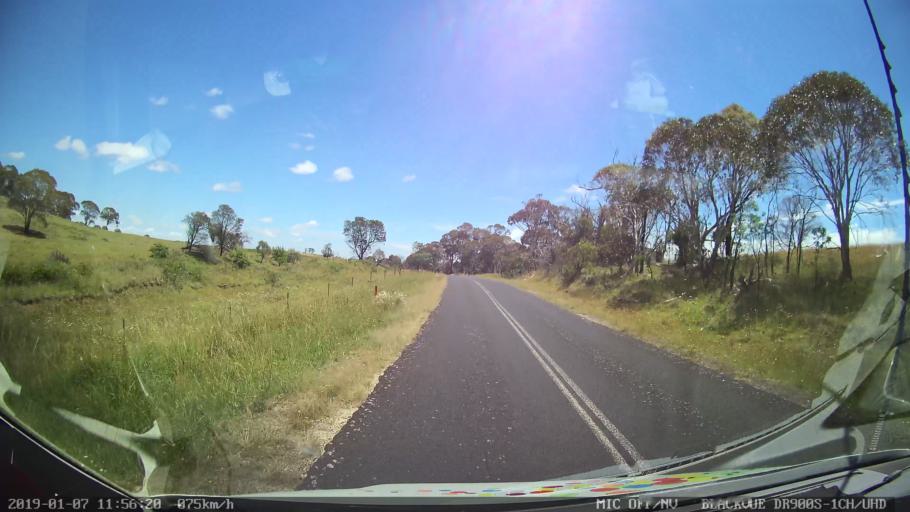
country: AU
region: New South Wales
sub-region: Guyra
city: Guyra
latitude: -30.2757
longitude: 151.6739
